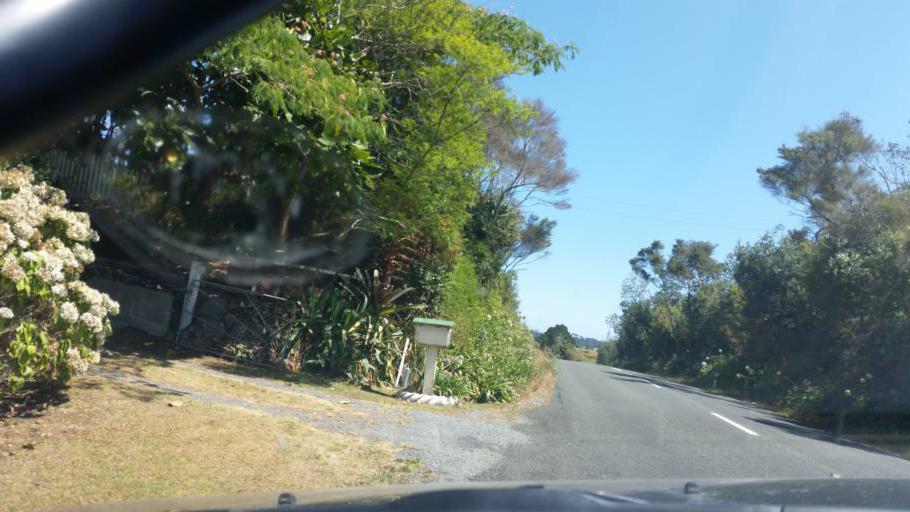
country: NZ
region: Northland
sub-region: Kaipara District
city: Dargaville
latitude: -36.0125
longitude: 173.9365
